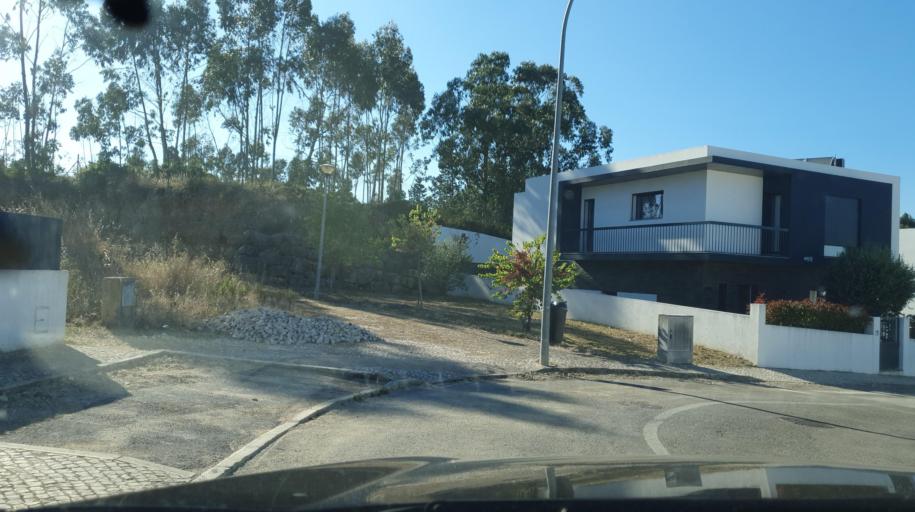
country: PT
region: Lisbon
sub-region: Sintra
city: Belas
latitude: 38.8046
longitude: -9.2544
